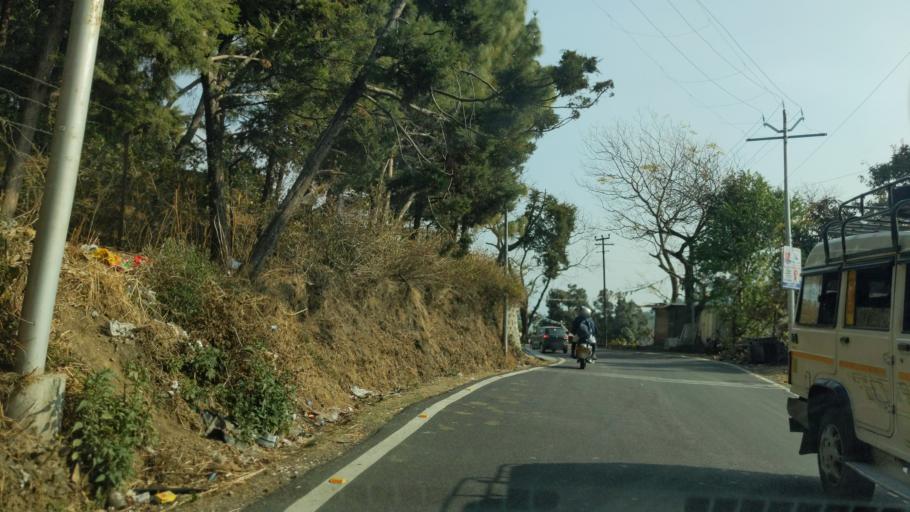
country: IN
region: Uttarakhand
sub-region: Naini Tal
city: Bhowali
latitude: 29.3787
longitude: 79.5259
